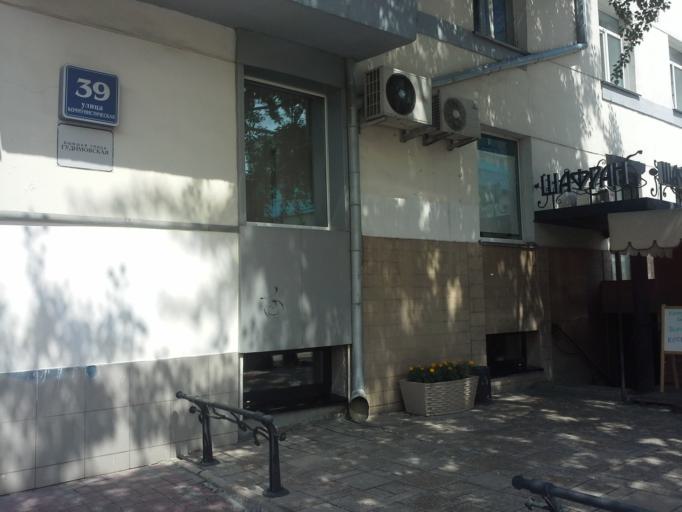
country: RU
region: Novosibirsk
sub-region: Novosibirskiy Rayon
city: Novosibirsk
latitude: 55.0237
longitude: 82.9227
